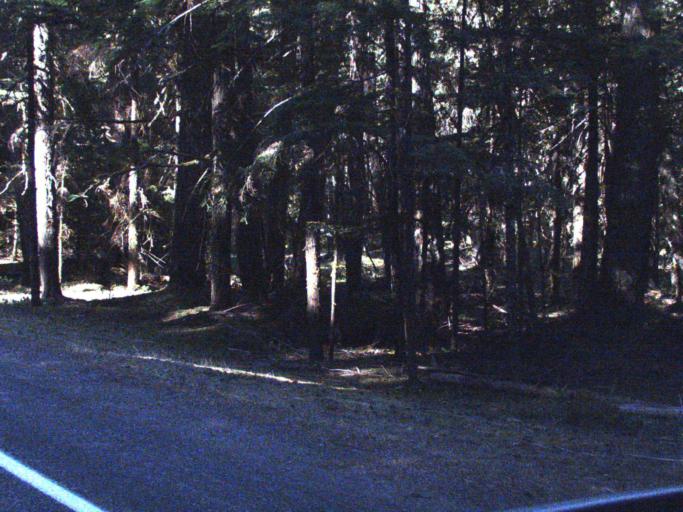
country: US
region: Washington
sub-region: King County
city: Enumclaw
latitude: 46.9899
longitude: -121.5332
